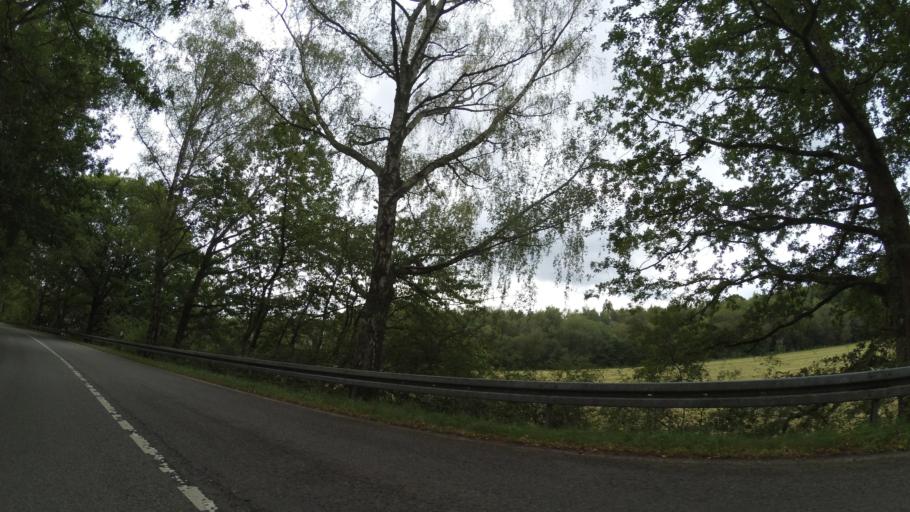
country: FR
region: Lorraine
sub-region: Departement de la Moselle
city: Petite-Rosselle
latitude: 49.2271
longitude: 6.8792
